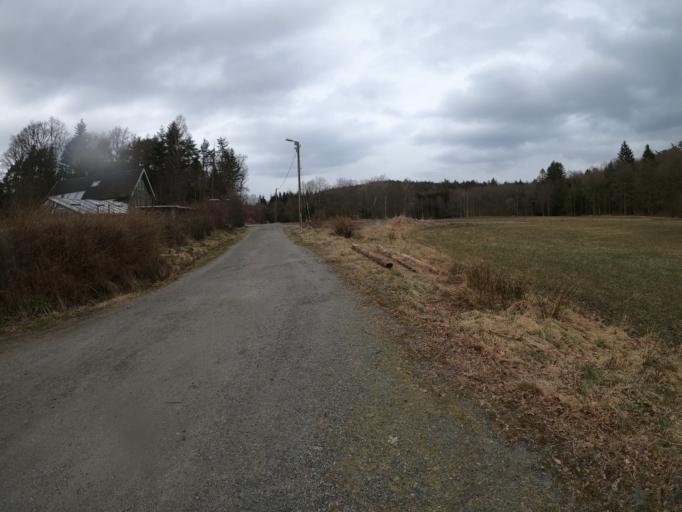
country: SE
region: Vaestra Goetaland
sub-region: Harryda Kommun
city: Molnlycke
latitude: 57.6245
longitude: 12.1072
